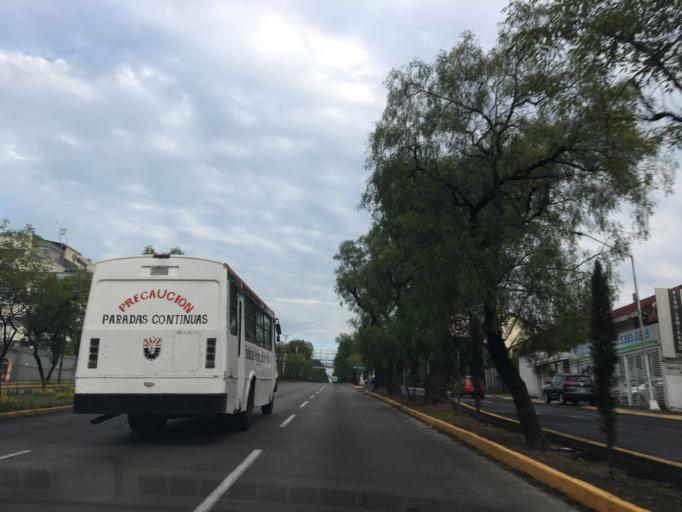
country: MX
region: Mexico
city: Naucalpan de Juarez
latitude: 19.5026
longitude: -99.2518
